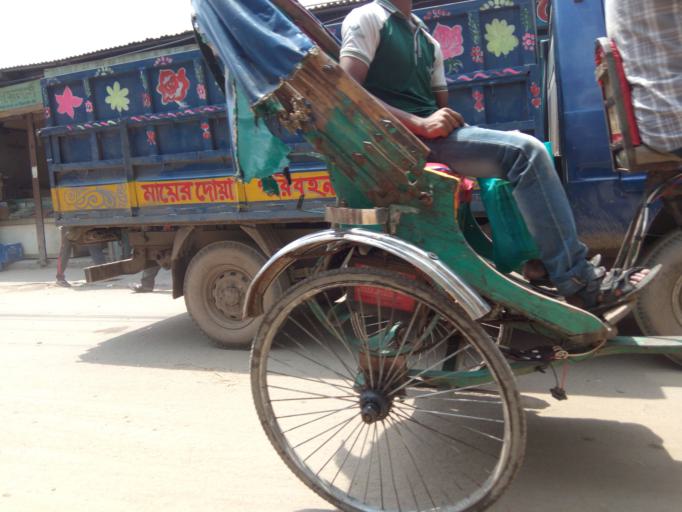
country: BD
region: Dhaka
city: Azimpur
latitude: 23.7118
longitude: 90.3798
